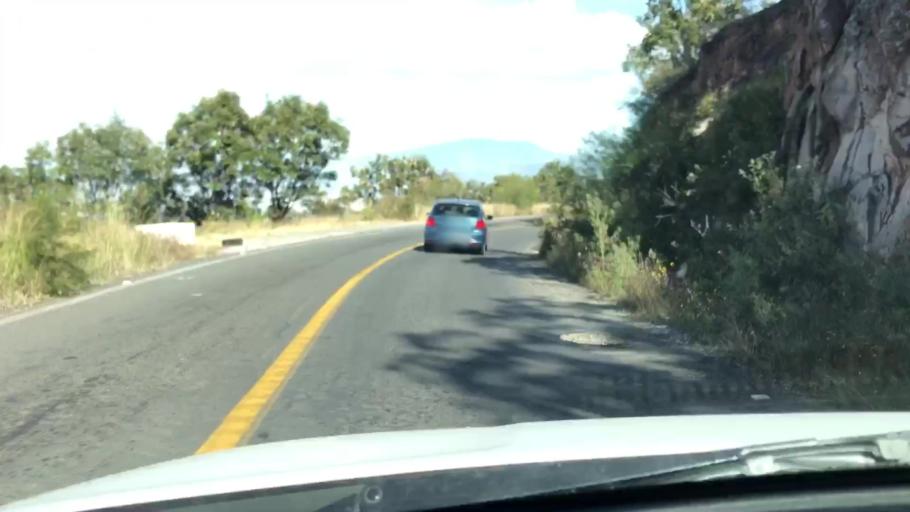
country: MX
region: Jalisco
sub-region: Zacoalco de Torres
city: Barranca de Otates (Barranca de Otatan)
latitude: 20.2014
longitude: -103.6928
